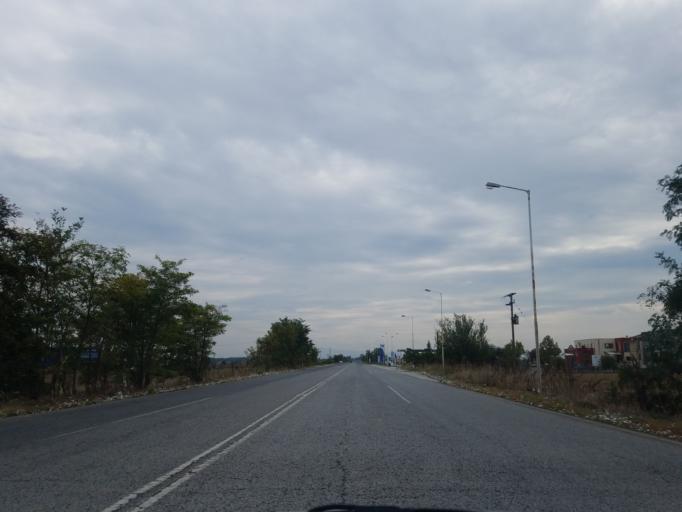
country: GR
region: Thessaly
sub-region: Nomos Kardhitsas
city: Sofades
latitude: 39.3495
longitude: 22.0674
